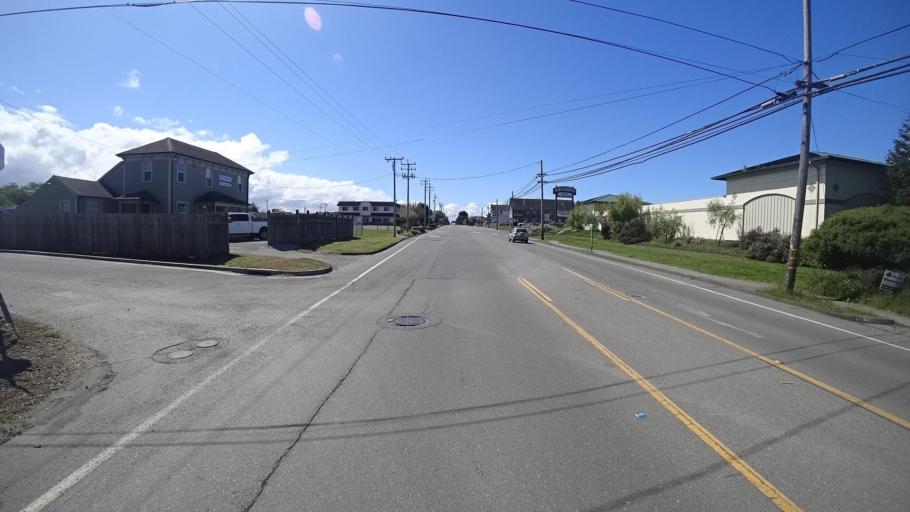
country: US
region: California
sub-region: Humboldt County
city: McKinleyville
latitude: 40.9490
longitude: -124.1009
